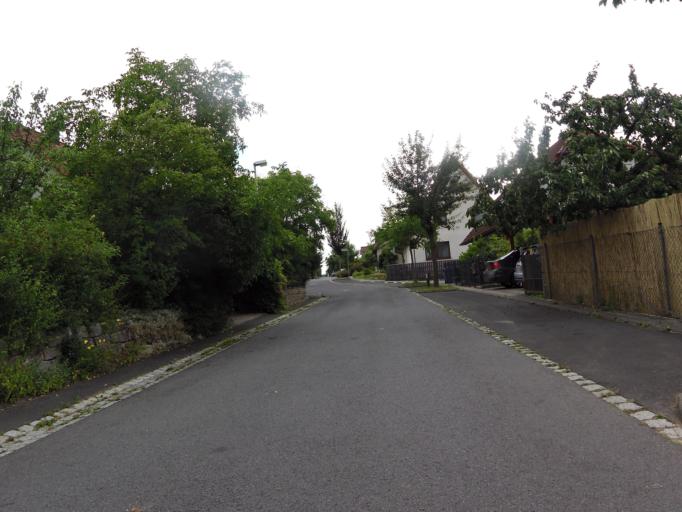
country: DE
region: Bavaria
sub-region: Regierungsbezirk Unterfranken
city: Eibelstadt
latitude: 49.7216
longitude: 9.9708
